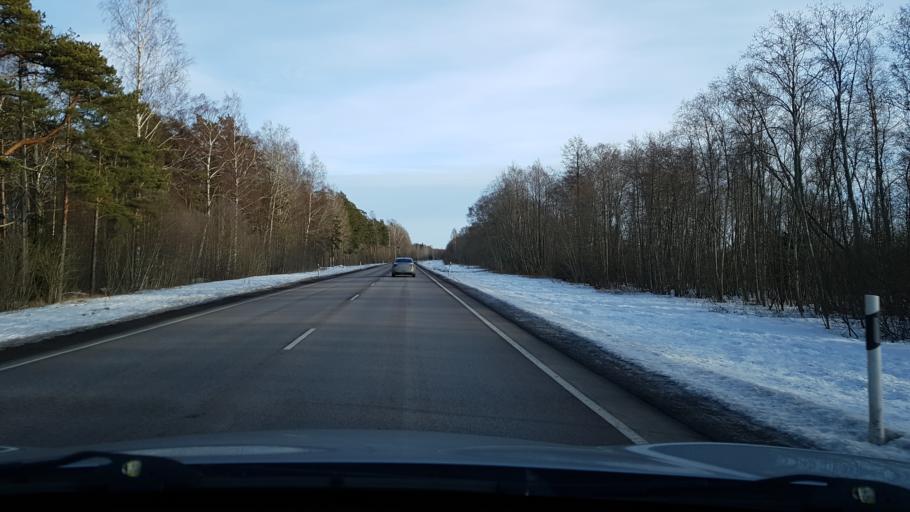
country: EE
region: Tartu
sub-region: Puhja vald
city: Puhja
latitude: 58.4014
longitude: 26.0962
